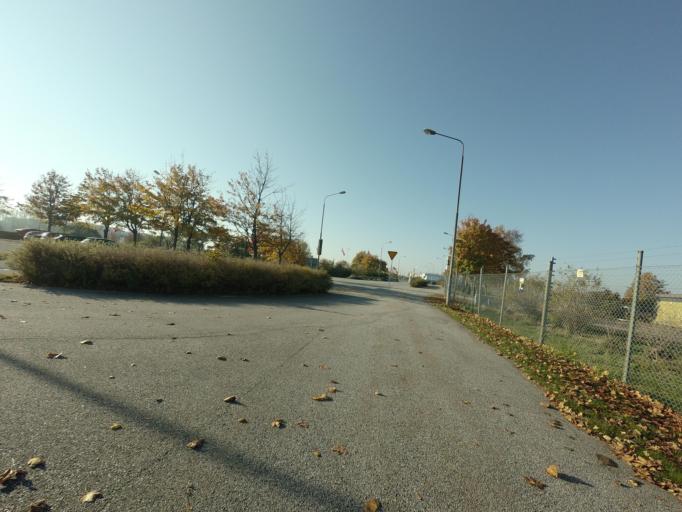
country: SE
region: Skane
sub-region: Burlovs Kommun
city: Arloev
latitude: 55.6435
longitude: 13.0866
